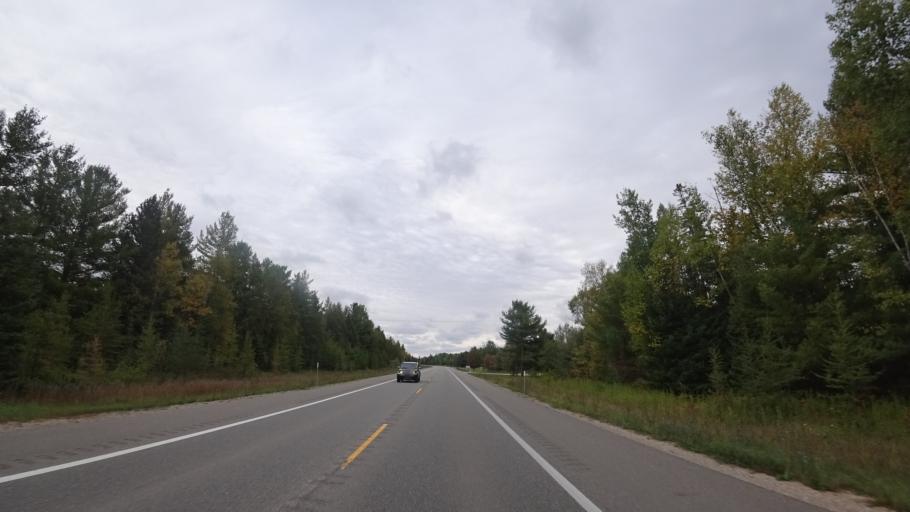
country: US
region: Michigan
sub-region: Charlevoix County
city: Boyne City
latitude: 45.1538
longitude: -84.9188
